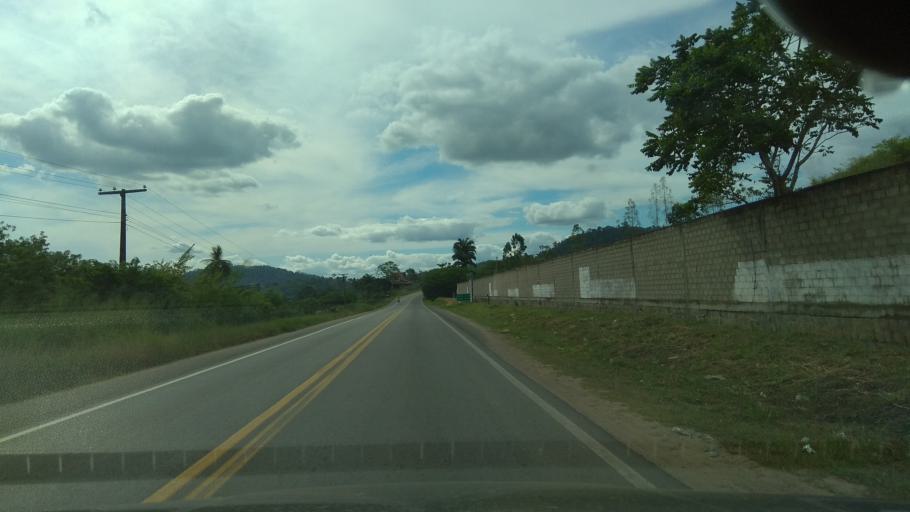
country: BR
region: Bahia
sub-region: Ipiau
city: Ipiau
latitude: -14.1158
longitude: -39.7722
